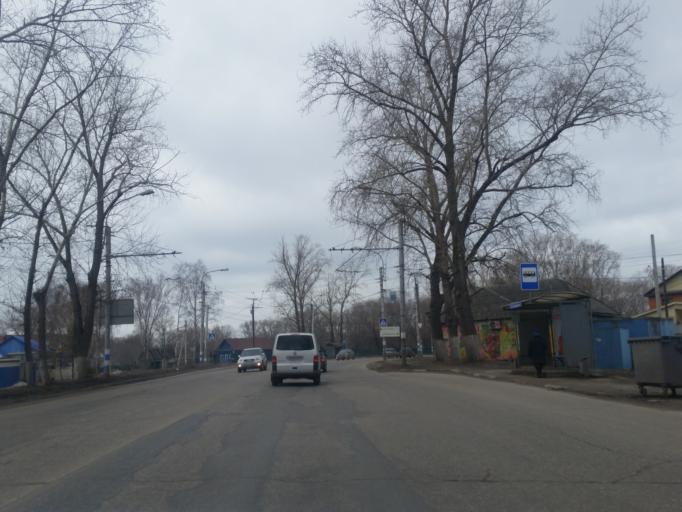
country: RU
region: Ulyanovsk
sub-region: Ulyanovskiy Rayon
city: Ulyanovsk
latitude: 54.3301
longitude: 48.4994
